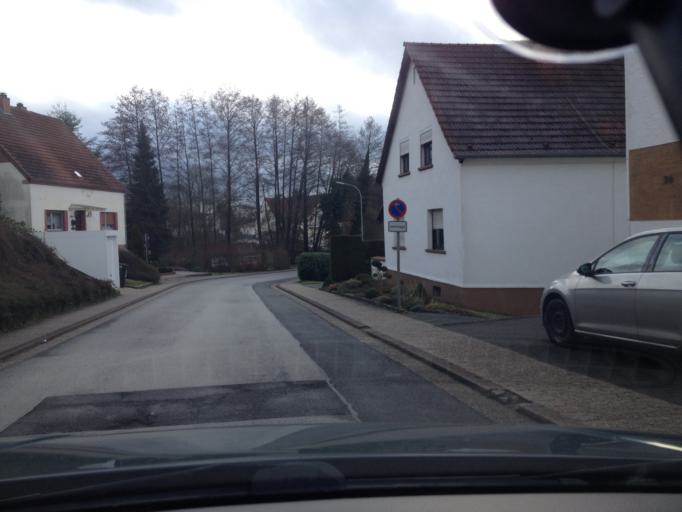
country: DE
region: Saarland
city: Sankt Wendel
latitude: 49.4980
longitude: 7.1603
